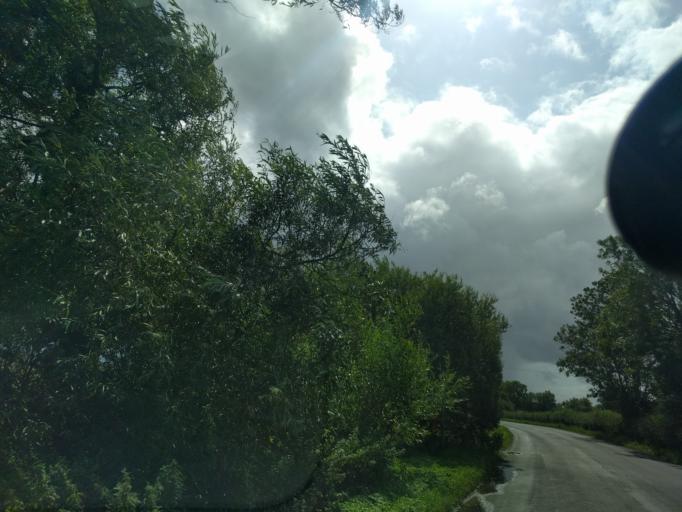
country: GB
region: England
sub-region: Wiltshire
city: Lyneham
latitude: 51.5274
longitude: -2.0135
